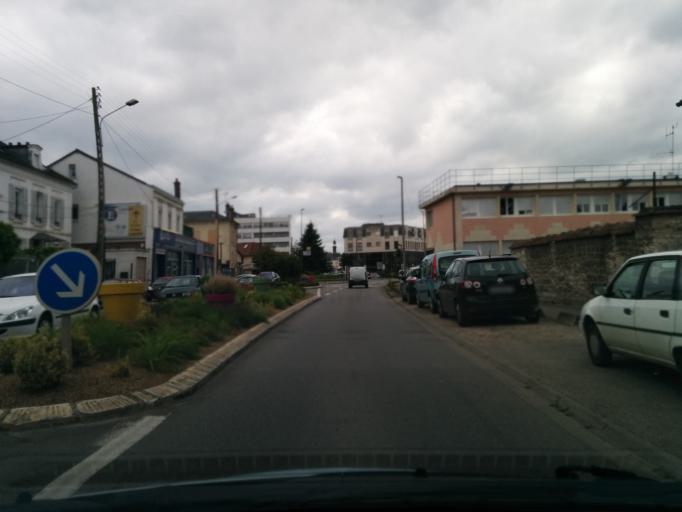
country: FR
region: Haute-Normandie
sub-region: Departement de l'Eure
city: Vernon
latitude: 49.0898
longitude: 1.4908
